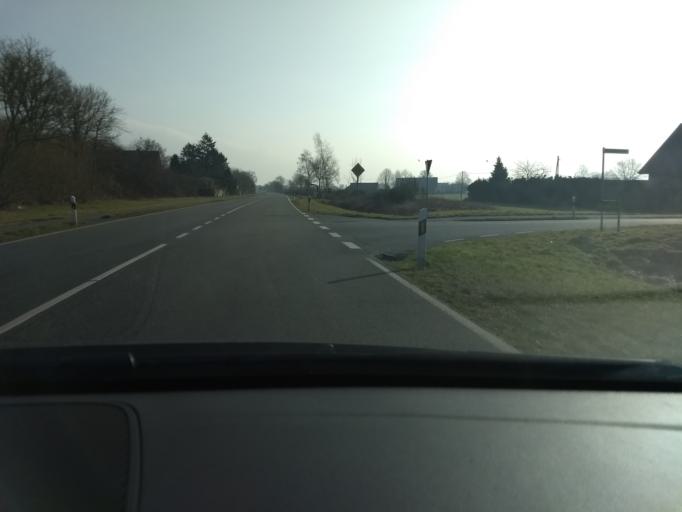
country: DE
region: North Rhine-Westphalia
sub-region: Regierungsbezirk Munster
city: Borken
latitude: 51.8314
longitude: 6.7928
